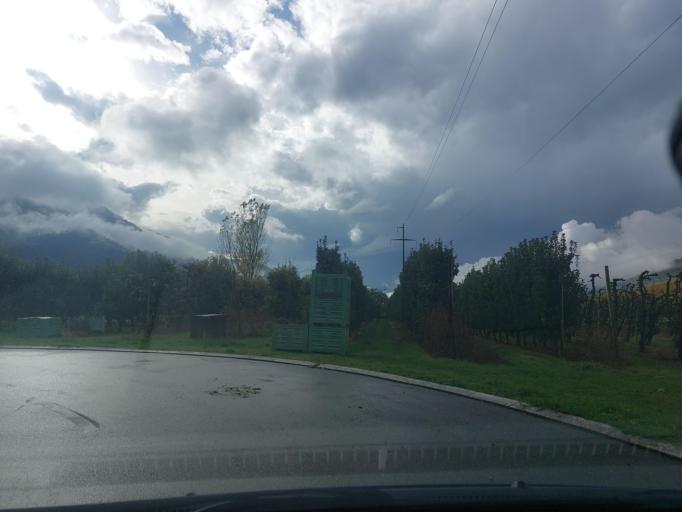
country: CH
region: Valais
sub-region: Sierre District
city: Chalais
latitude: 46.2731
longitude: 7.5148
